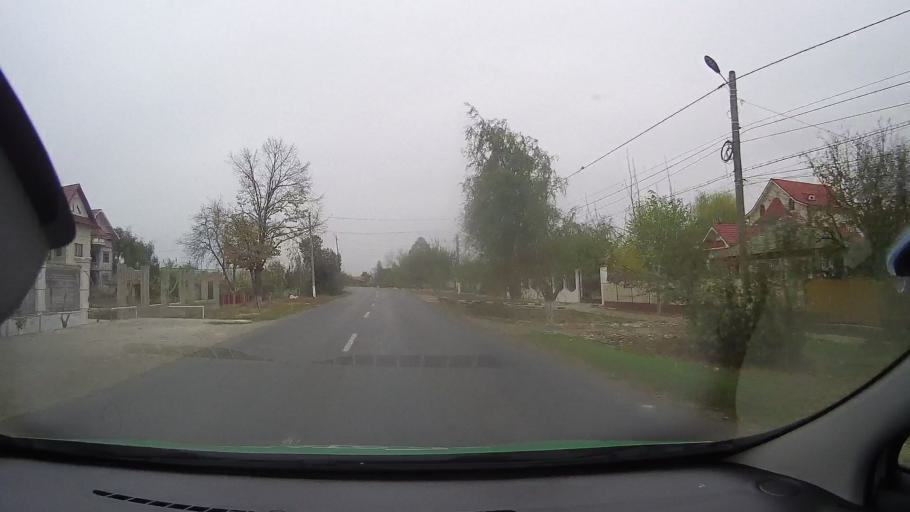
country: RO
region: Ialomita
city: Tandarei
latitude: 44.6523
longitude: 27.6548
